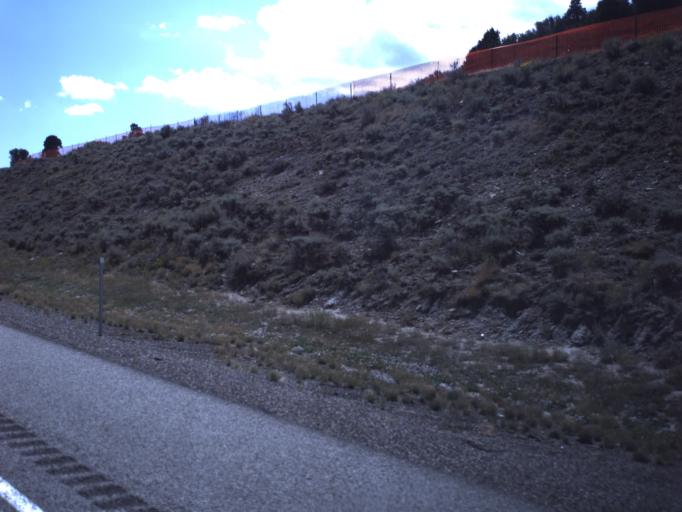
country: US
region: Utah
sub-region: Wayne County
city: Loa
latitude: 38.7813
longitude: -111.4866
